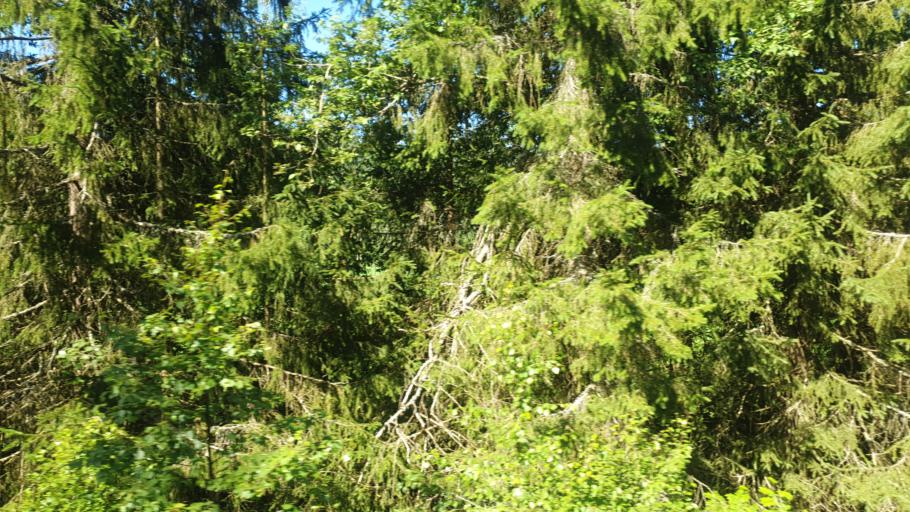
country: NO
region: Sor-Trondelag
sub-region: Meldal
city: Meldal
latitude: 63.1816
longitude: 9.7681
